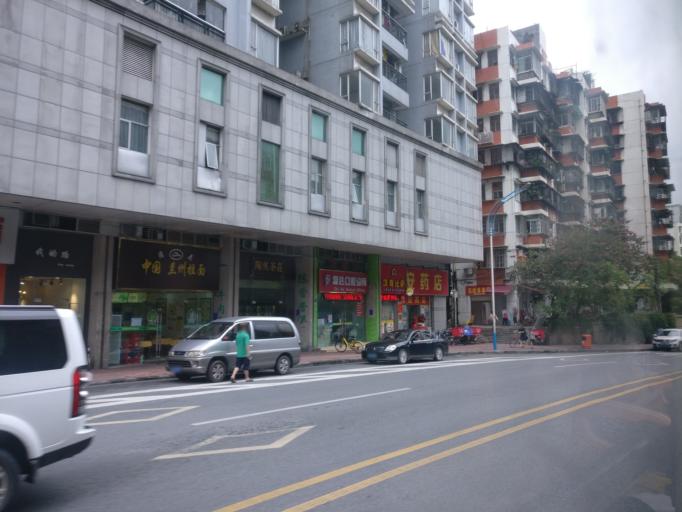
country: CN
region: Guangdong
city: Guangzhou
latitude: 23.1478
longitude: 113.2706
